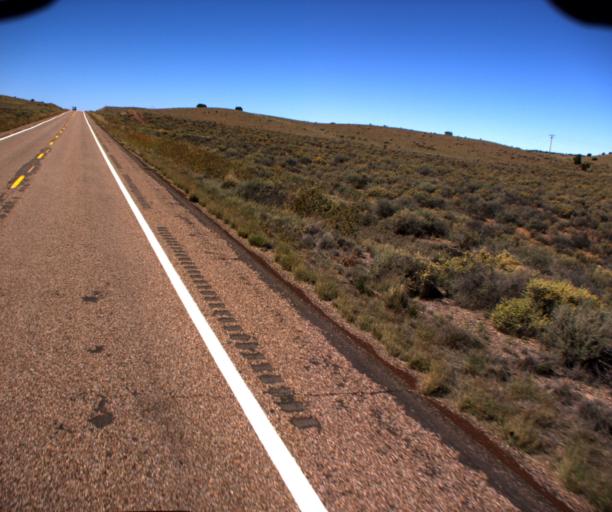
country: US
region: Arizona
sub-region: Apache County
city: Saint Johns
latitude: 34.5861
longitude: -109.5809
